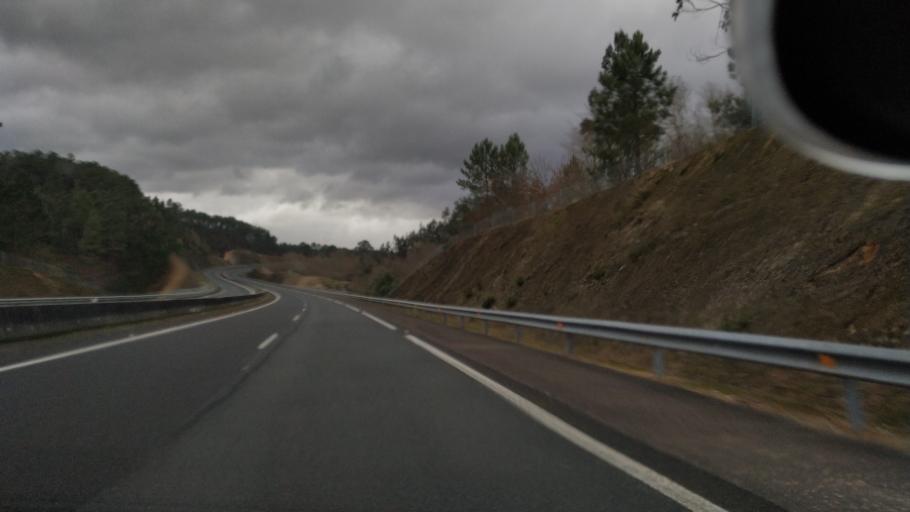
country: ES
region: Galicia
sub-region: Provincia da Coruna
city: Vedra
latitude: 42.7914
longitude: -8.4798
